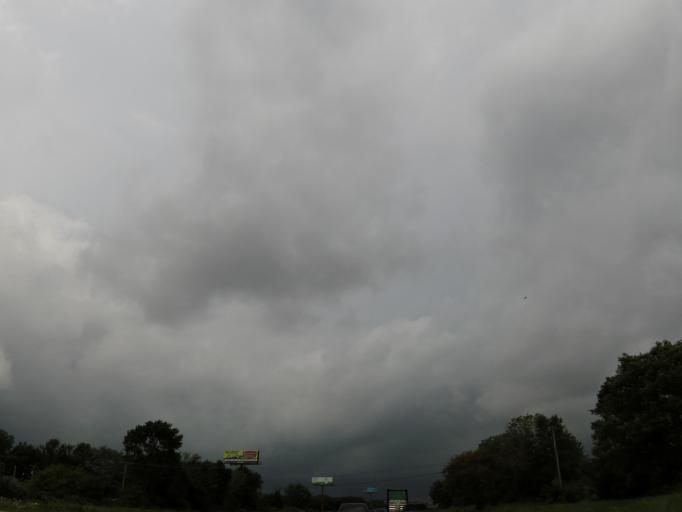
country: US
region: Illinois
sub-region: Jefferson County
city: Ina
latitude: 38.2013
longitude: -88.9098
